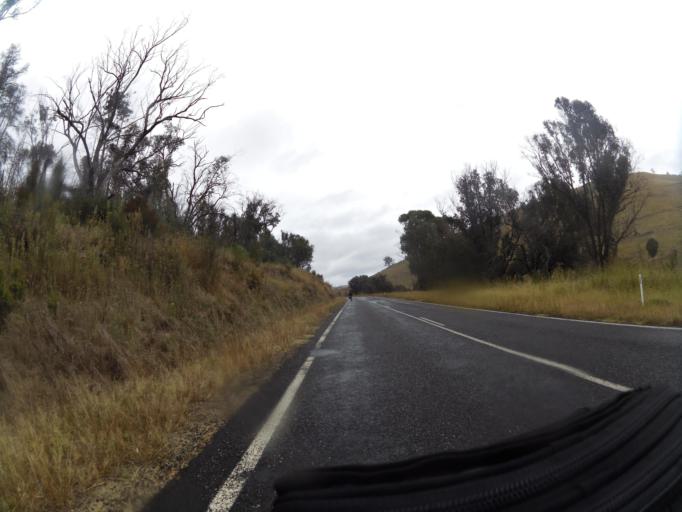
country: AU
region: New South Wales
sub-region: Greater Hume Shire
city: Holbrook
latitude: -36.2241
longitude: 147.7265
